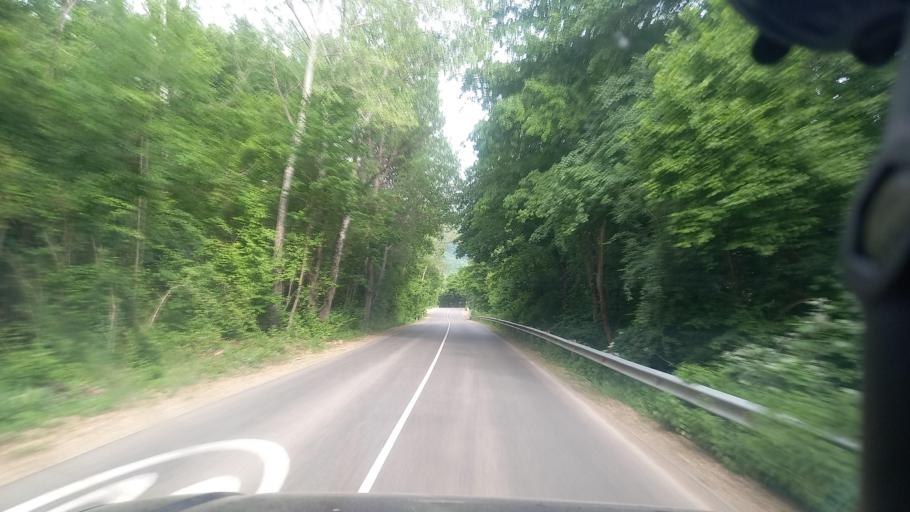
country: RU
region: Krasnodarskiy
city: Goryachiy Klyuch
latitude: 44.6026
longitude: 39.0395
